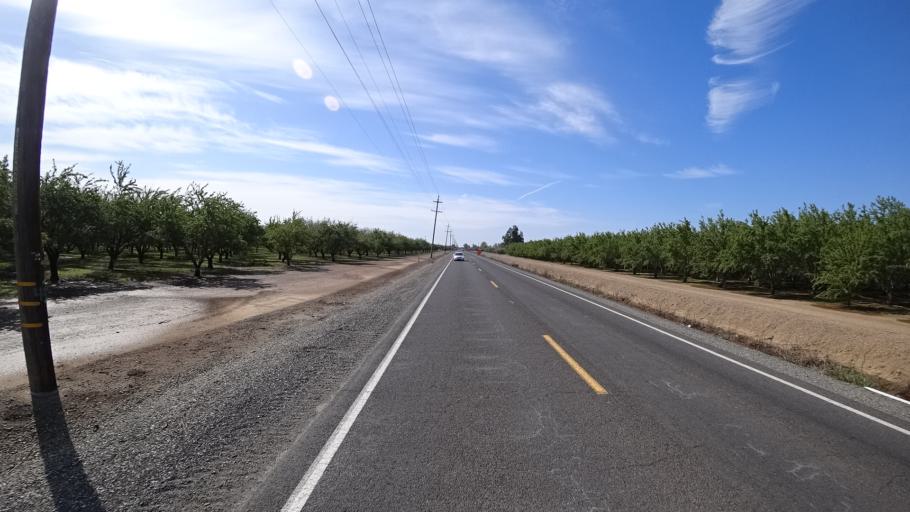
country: US
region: California
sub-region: Glenn County
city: Hamilton City
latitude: 39.6577
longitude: -122.0081
